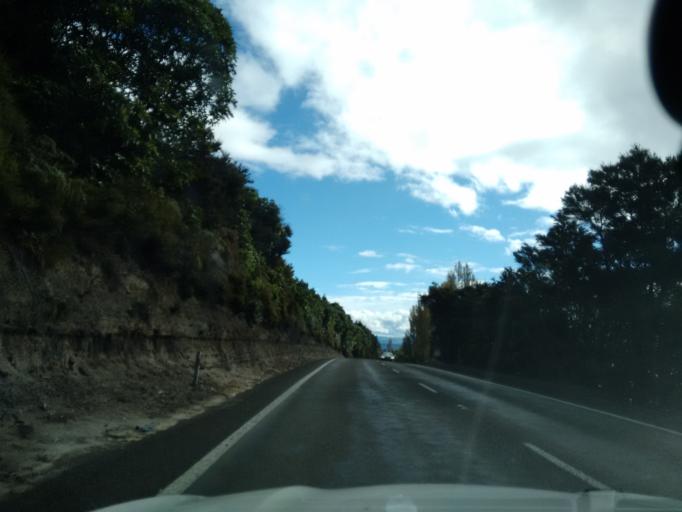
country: NZ
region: Waikato
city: Turangi
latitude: -38.8800
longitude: 175.9771
